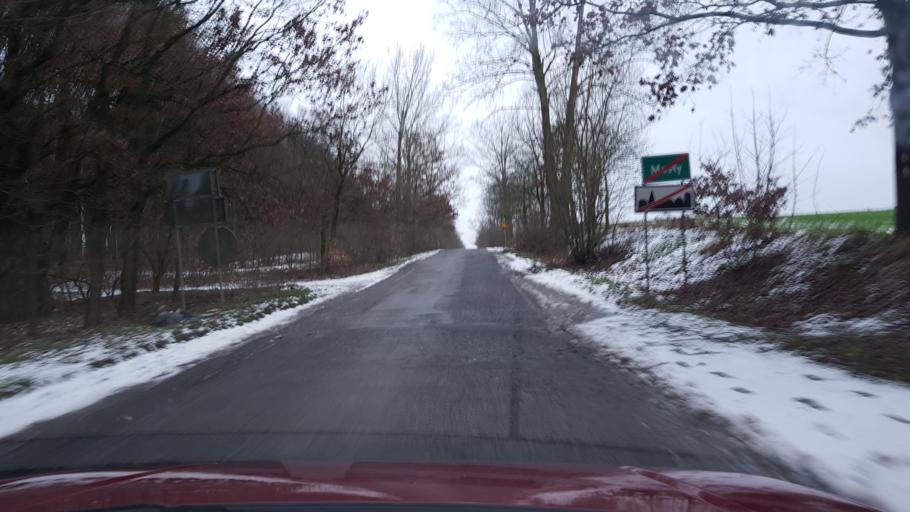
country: PL
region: West Pomeranian Voivodeship
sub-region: Powiat goleniowski
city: Mosty
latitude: 53.5442
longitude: 14.9538
